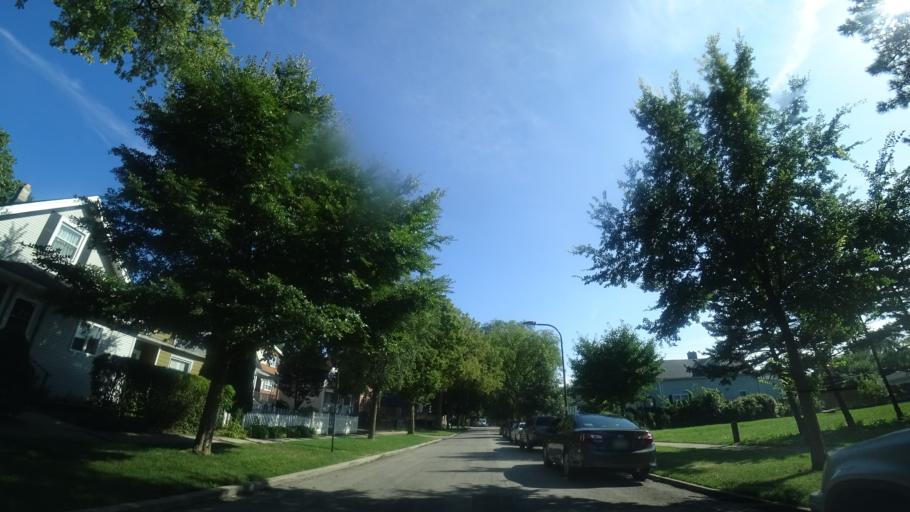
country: US
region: Illinois
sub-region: Cook County
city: Evanston
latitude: 42.0568
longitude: -87.6973
